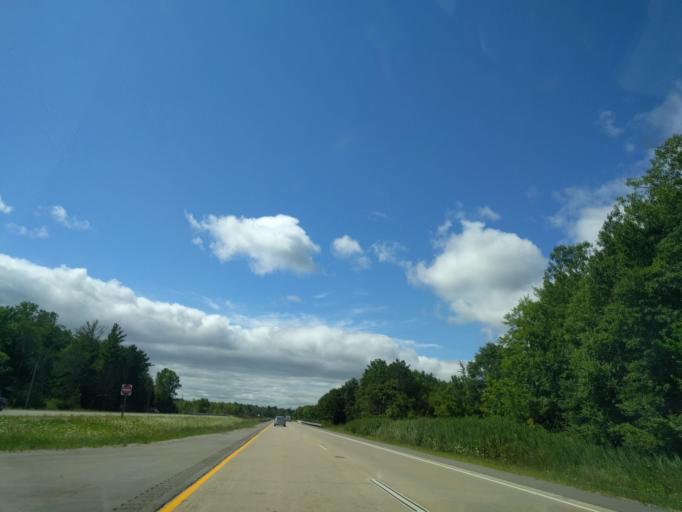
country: US
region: Wisconsin
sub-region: Oconto County
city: Oconto
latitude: 44.8224
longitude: -87.9368
